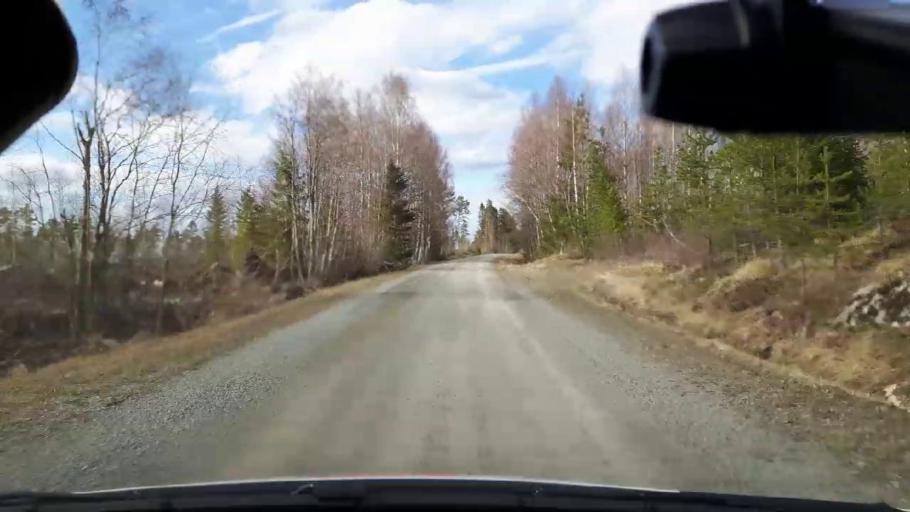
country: SE
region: Jaemtland
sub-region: Bergs Kommun
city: Hoverberg
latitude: 62.7513
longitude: 14.6628
